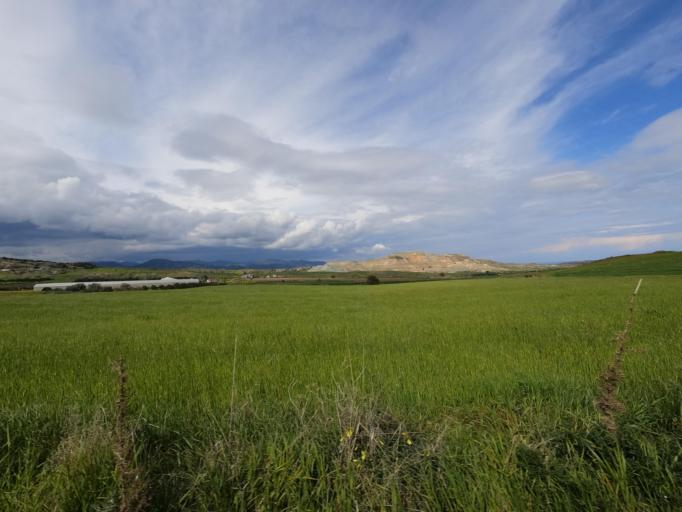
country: CY
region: Lefkosia
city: Lefka
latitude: 35.0826
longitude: 32.9258
